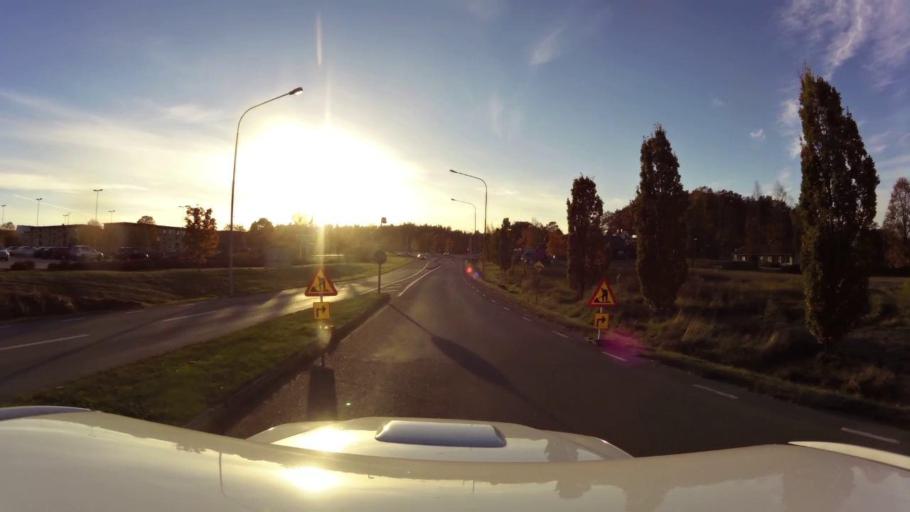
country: SE
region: OEstergoetland
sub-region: Linkopings Kommun
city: Linkoping
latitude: 58.3870
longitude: 15.6780
